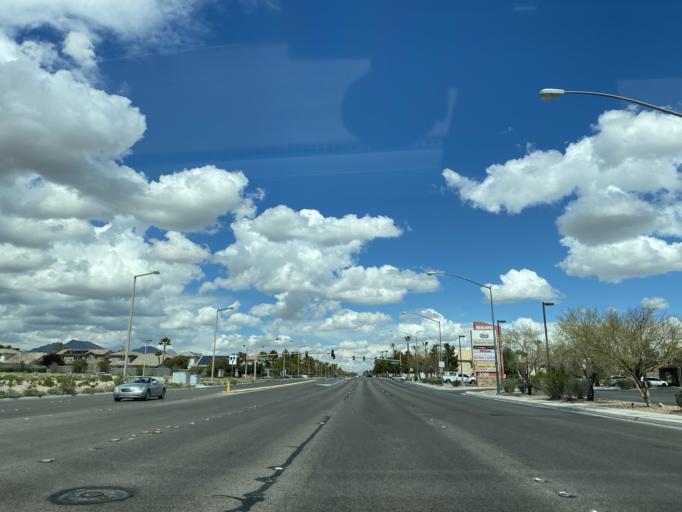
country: US
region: Nevada
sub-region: Clark County
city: Summerlin South
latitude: 36.1211
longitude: -115.3149
